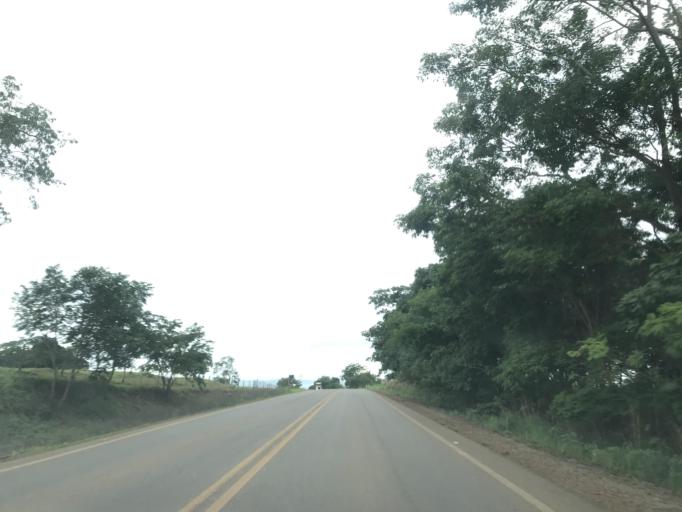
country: BR
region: Goias
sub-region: Vianopolis
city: Vianopolis
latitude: -16.7098
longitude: -48.3986
